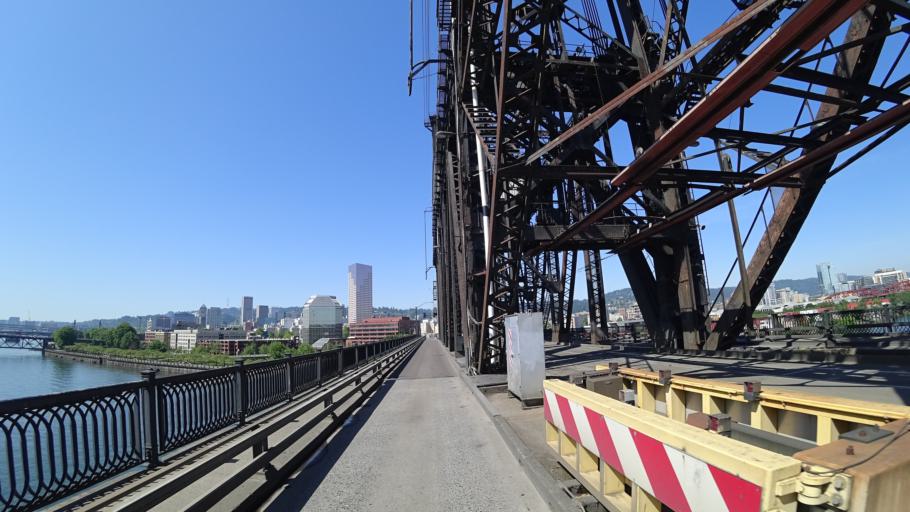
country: US
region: Oregon
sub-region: Multnomah County
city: Portland
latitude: 45.5278
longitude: -122.6686
